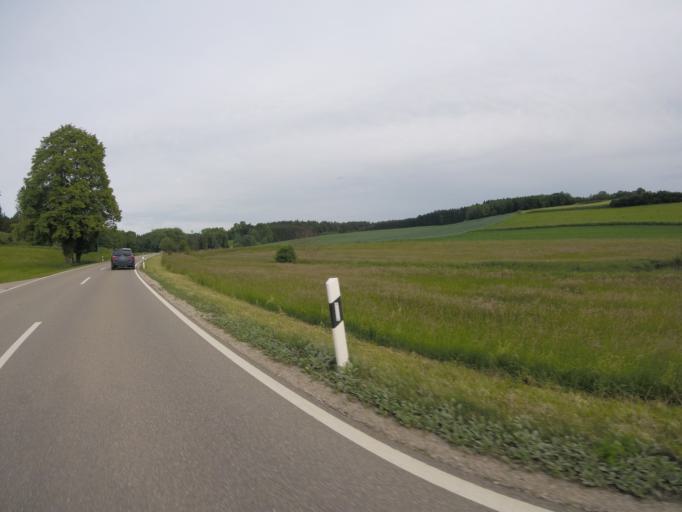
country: DE
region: Bavaria
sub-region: Upper Bavaria
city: Ilmmunster
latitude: 48.4835
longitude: 11.5142
